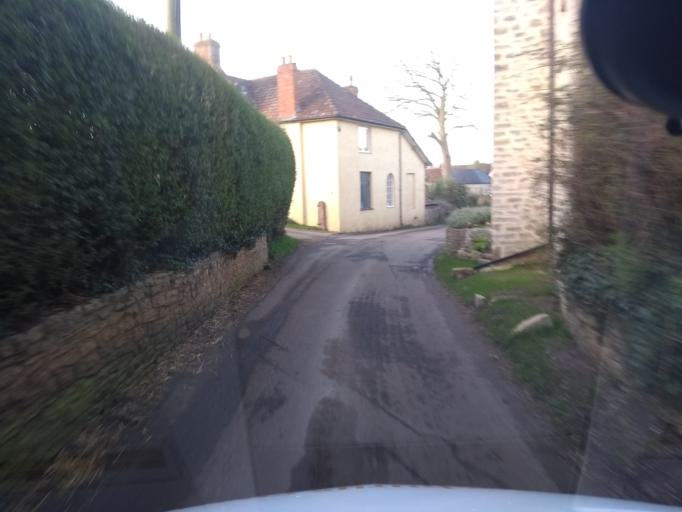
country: GB
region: England
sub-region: Somerset
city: Wedmore
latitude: 51.2271
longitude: -2.8417
